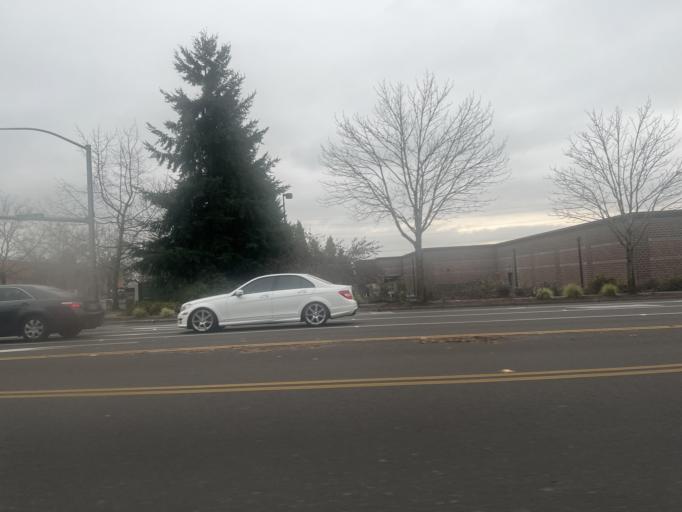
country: US
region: Oregon
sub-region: Clackamas County
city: Wilsonville
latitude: 45.3357
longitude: -122.7619
